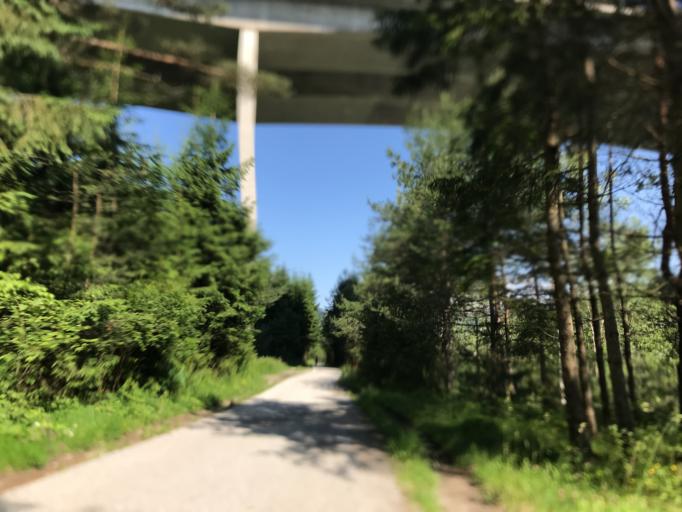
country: AT
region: Carinthia
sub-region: Politischer Bezirk Villach Land
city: Finkenstein am Faaker See
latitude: 46.5761
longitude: 13.8406
